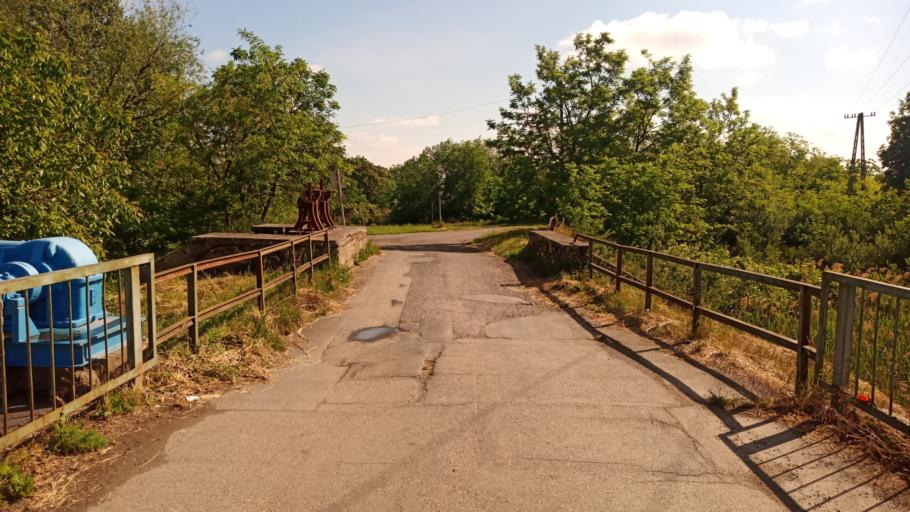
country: HU
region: Bekes
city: Bekes
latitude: 46.7859
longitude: 21.1236
